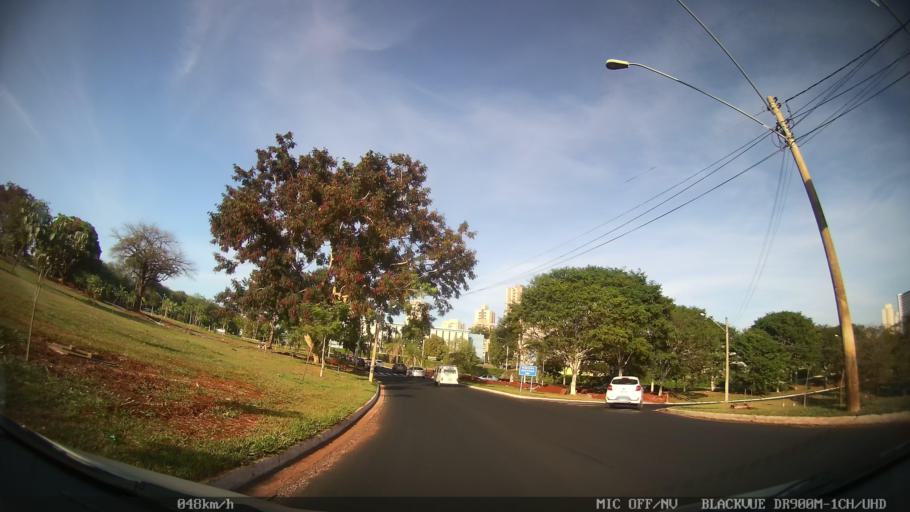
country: BR
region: Sao Paulo
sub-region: Ribeirao Preto
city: Ribeirao Preto
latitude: -21.2175
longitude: -47.8157
